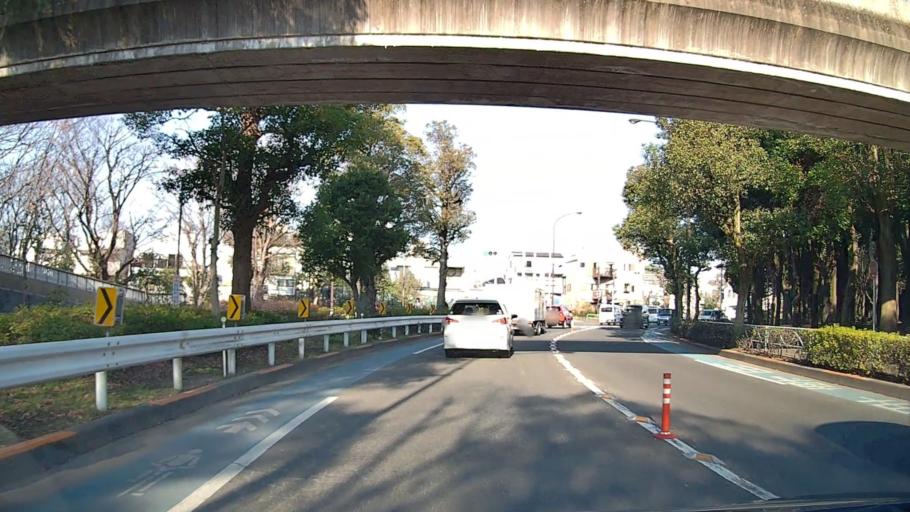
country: JP
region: Saitama
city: Wako
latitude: 35.7695
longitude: 139.6260
